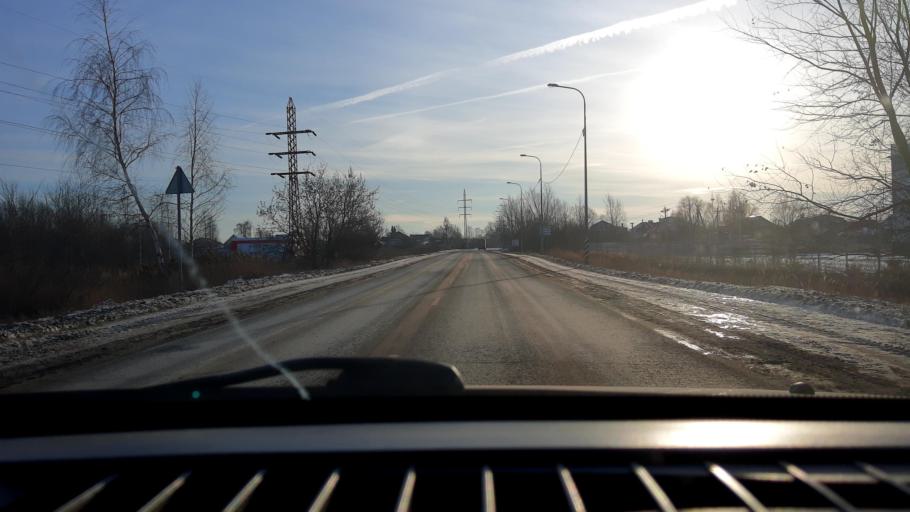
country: RU
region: Nizjnij Novgorod
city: Bor
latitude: 56.3754
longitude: 44.0604
